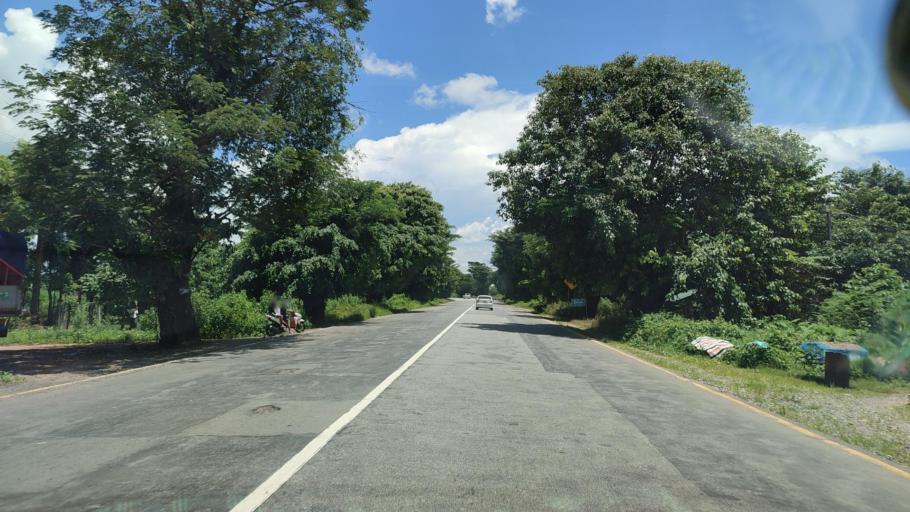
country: MM
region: Bago
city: Nyaunglebin
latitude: 18.1879
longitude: 96.5733
